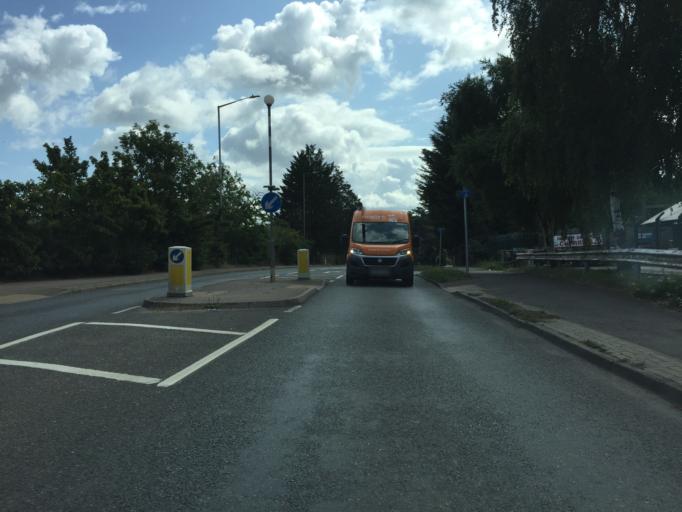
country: GB
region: England
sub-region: Kent
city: Aylesford
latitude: 51.2955
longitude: 0.4686
